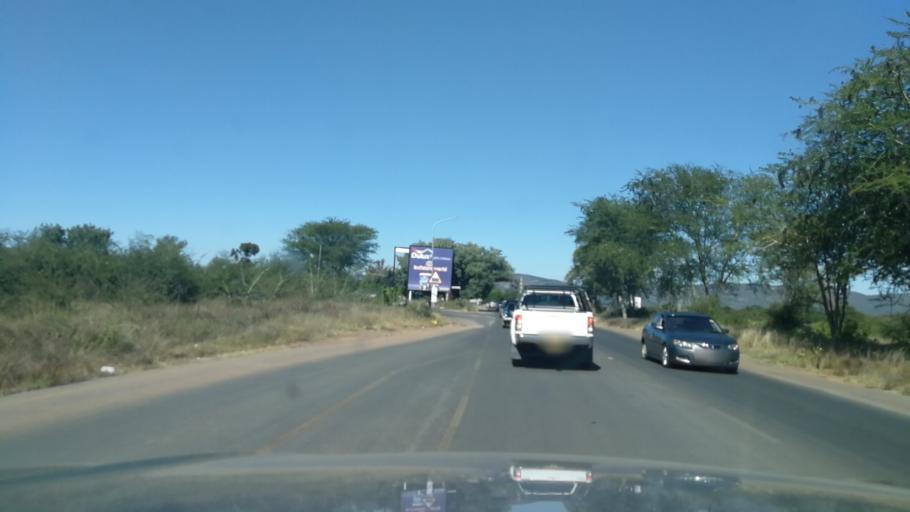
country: BW
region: South East
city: Gaborone
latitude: -24.6919
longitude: 25.8892
